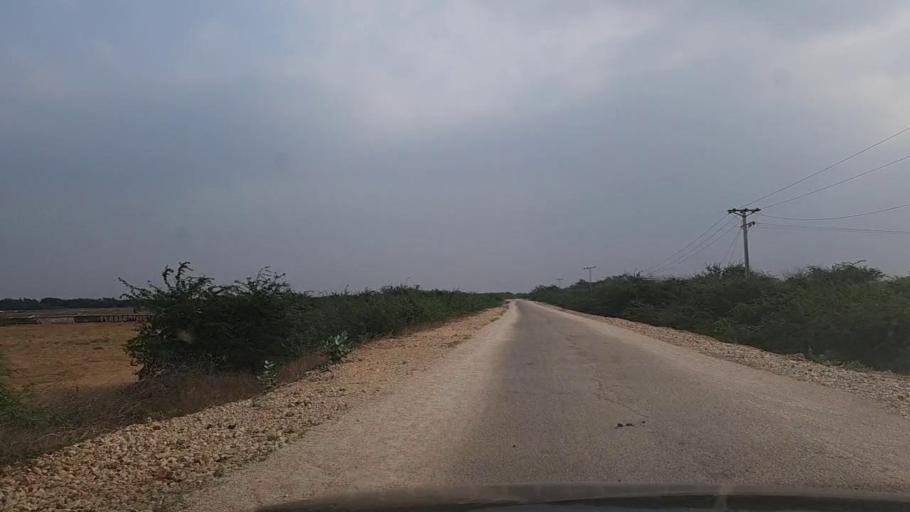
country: PK
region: Sindh
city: Thatta
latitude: 24.8514
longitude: 67.7773
